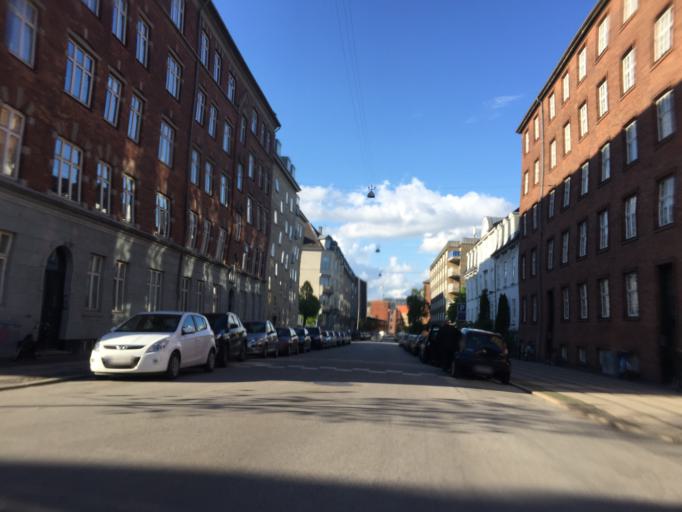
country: DK
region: Capital Region
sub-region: Frederiksberg Kommune
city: Frederiksberg
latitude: 55.6877
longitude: 12.5328
